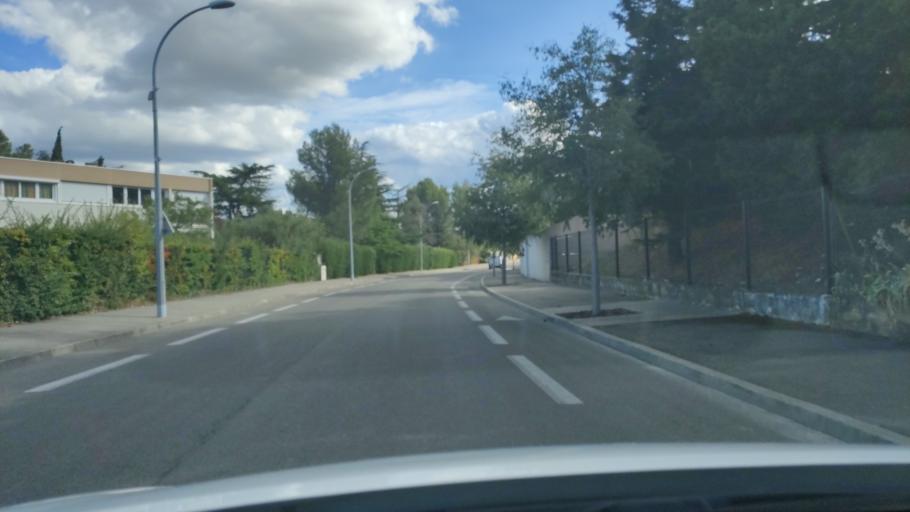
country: FR
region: Languedoc-Roussillon
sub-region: Departement du Gard
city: Villeneuve-les-Avignon
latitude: 43.9740
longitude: 4.7766
